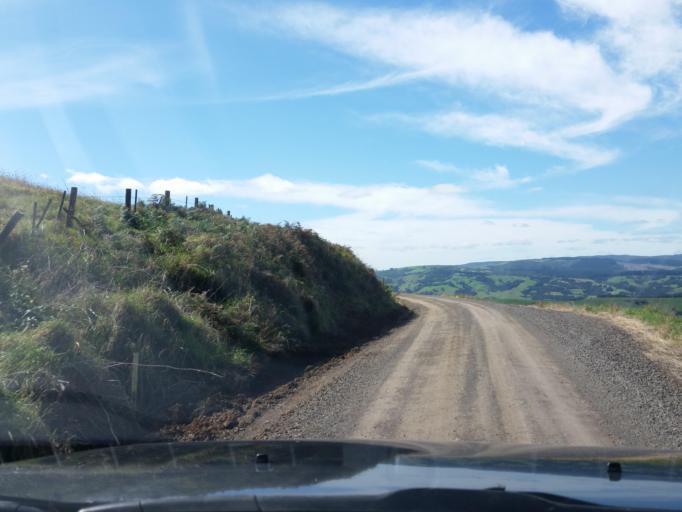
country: NZ
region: Northland
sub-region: Kaipara District
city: Dargaville
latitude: -35.7250
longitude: 173.5748
